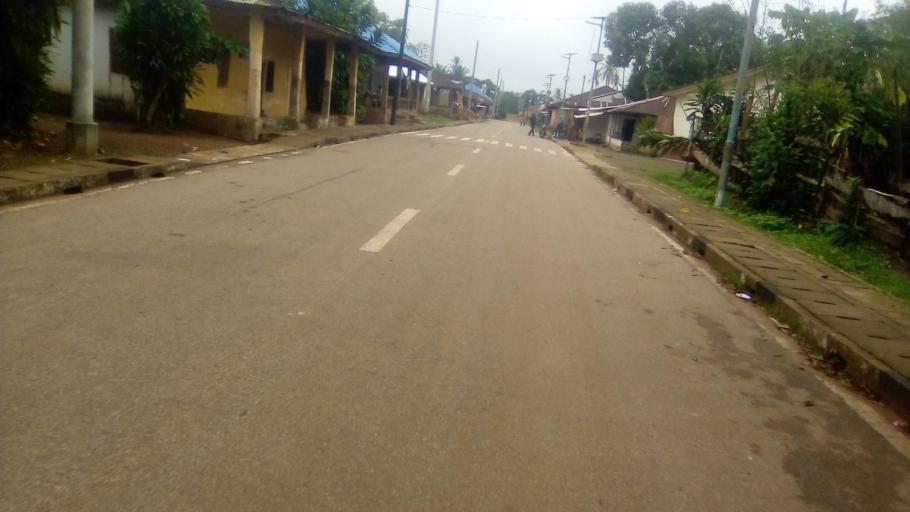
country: SL
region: Southern Province
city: Moyamba
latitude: 8.1617
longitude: -12.4338
